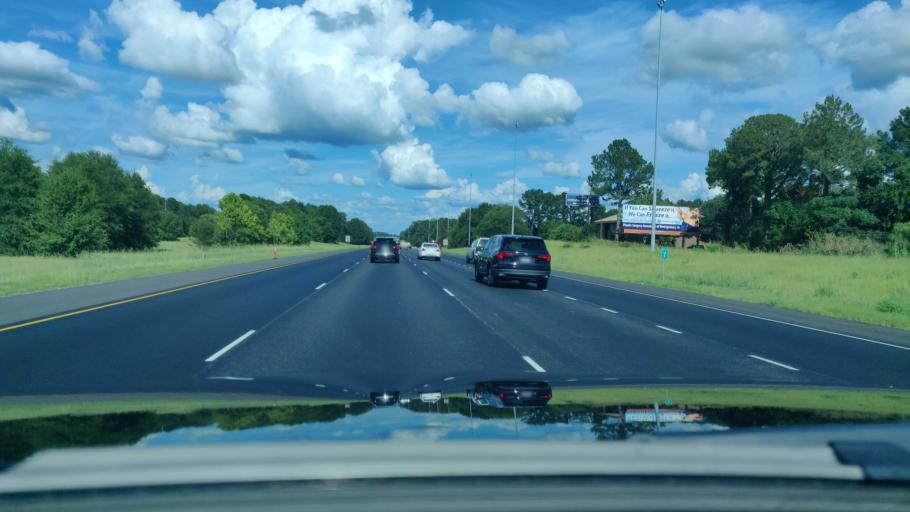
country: US
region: Alabama
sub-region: Montgomery County
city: Montgomery
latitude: 32.3622
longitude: -86.2063
